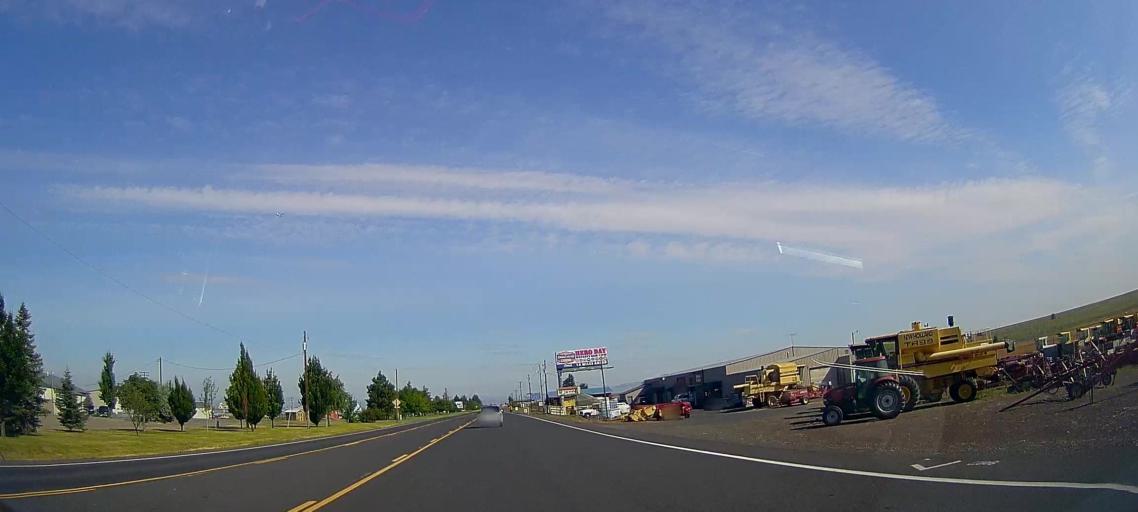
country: US
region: Oregon
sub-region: Jefferson County
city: Madras
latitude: 44.6580
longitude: -121.1311
